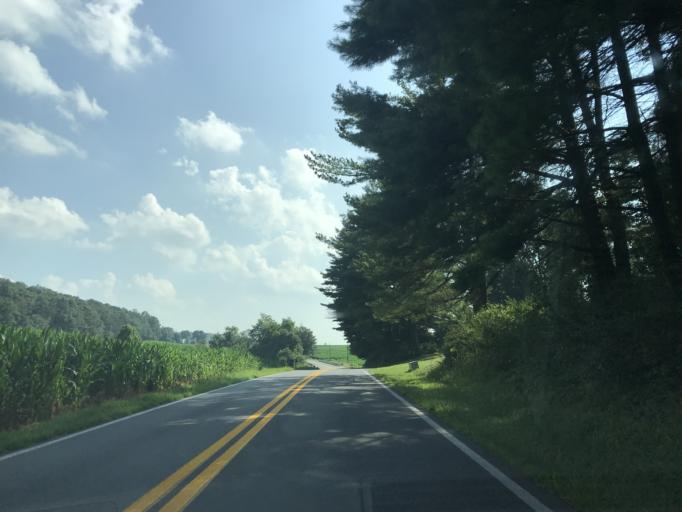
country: US
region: Maryland
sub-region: Carroll County
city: Manchester
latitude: 39.6506
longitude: -76.9343
